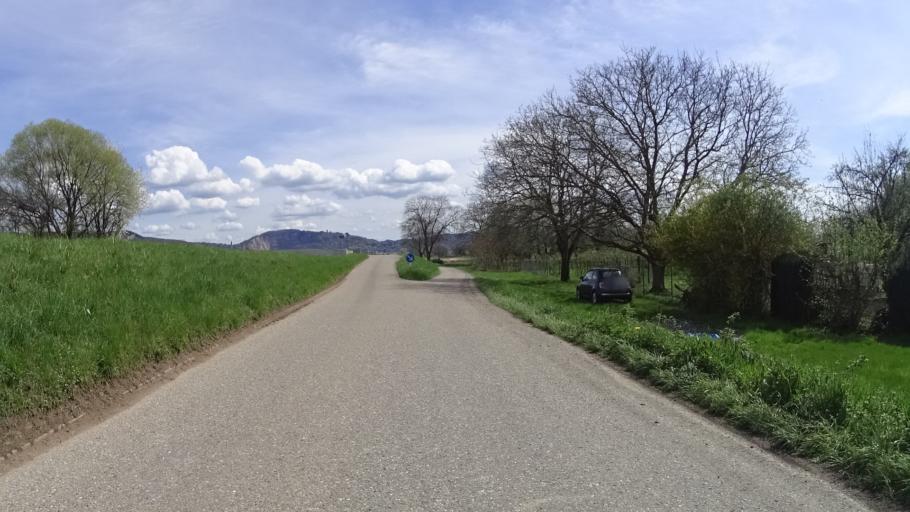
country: DE
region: Baden-Wuerttemberg
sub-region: Karlsruhe Region
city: Hemsbach
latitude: 49.5694
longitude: 8.6369
